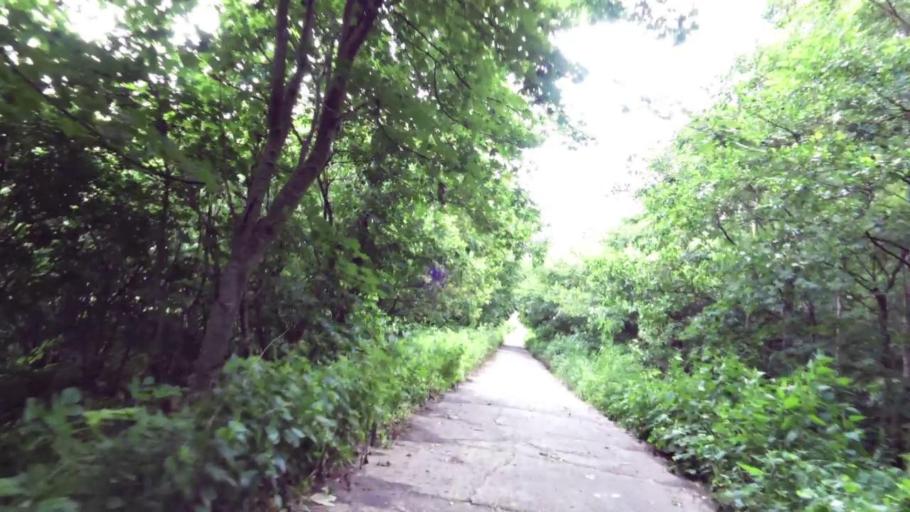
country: PL
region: West Pomeranian Voivodeship
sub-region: Powiat slawienski
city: Darlowo
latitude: 54.4922
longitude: 16.4416
